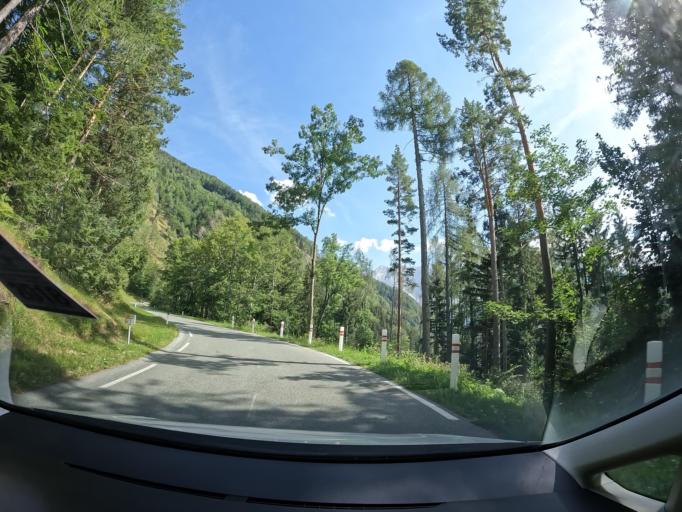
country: AT
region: Carinthia
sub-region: Politischer Bezirk Feldkirchen
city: Glanegg
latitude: 46.7249
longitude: 14.2391
